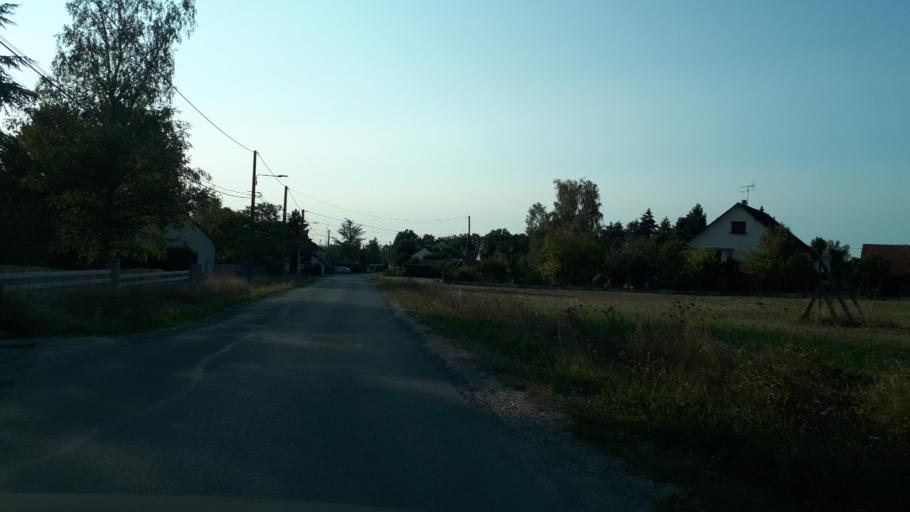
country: FR
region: Centre
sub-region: Departement du Loir-et-Cher
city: Romorantin-Lanthenay
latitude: 47.3430
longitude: 1.7727
